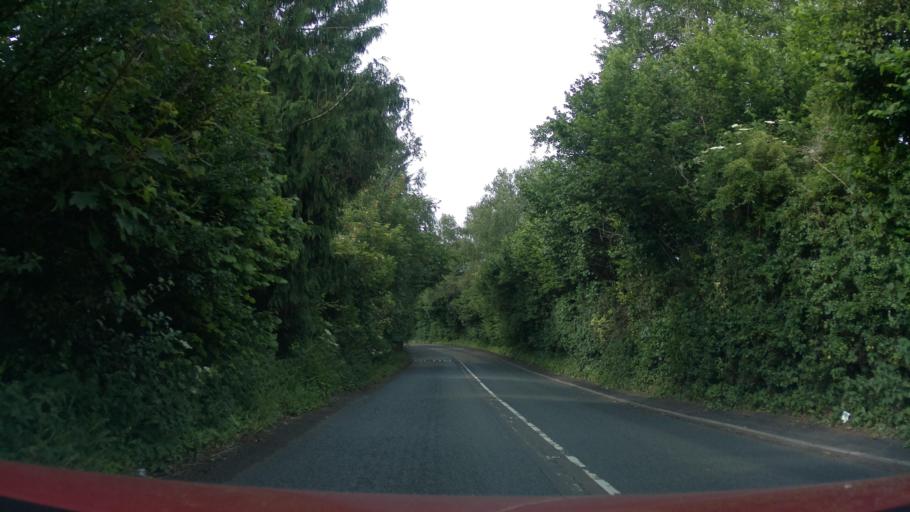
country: GB
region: England
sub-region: South Gloucestershire
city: Bitton
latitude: 51.4135
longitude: -2.4377
